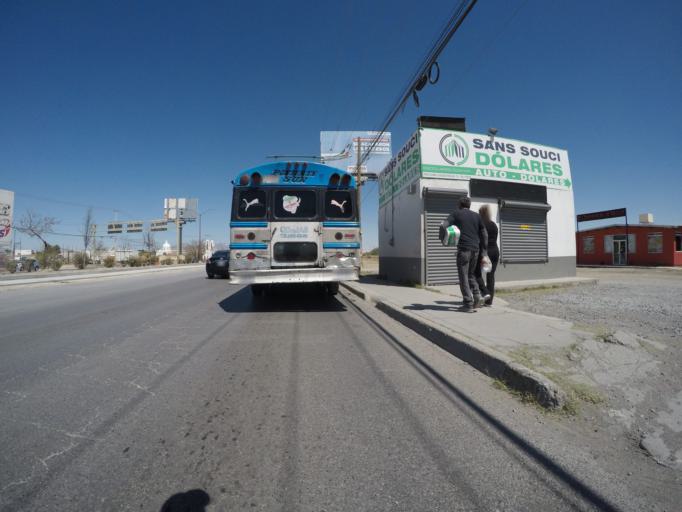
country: MX
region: Chihuahua
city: Ciudad Juarez
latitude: 31.6826
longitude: -106.4244
